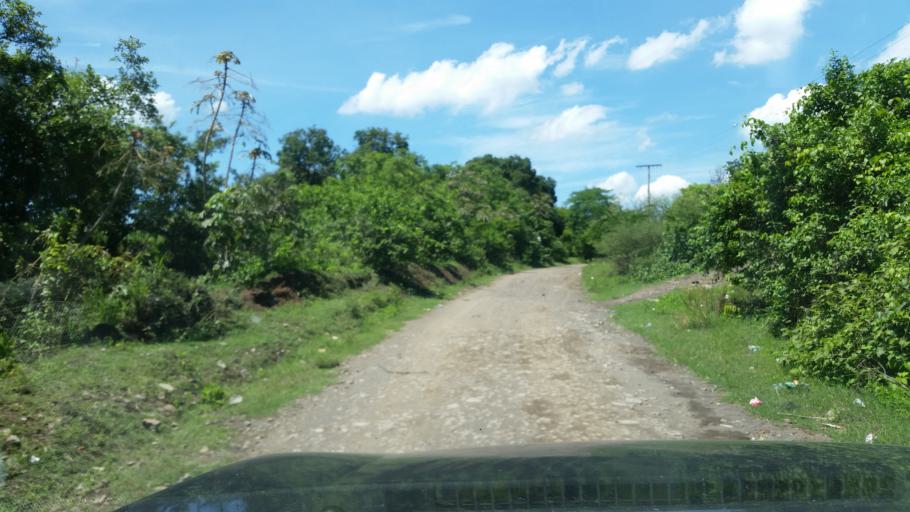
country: NI
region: Chinandega
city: Puerto Morazan
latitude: 12.7630
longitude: -87.1334
